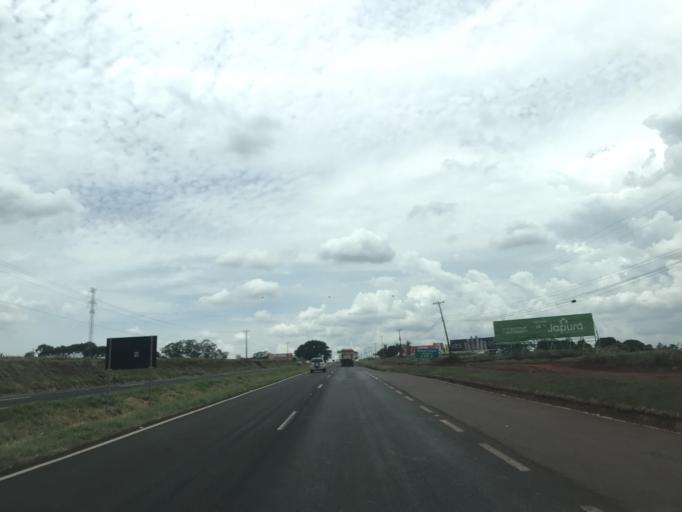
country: BR
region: Parana
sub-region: Maringa
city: Maringa
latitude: -23.3964
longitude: -52.0059
